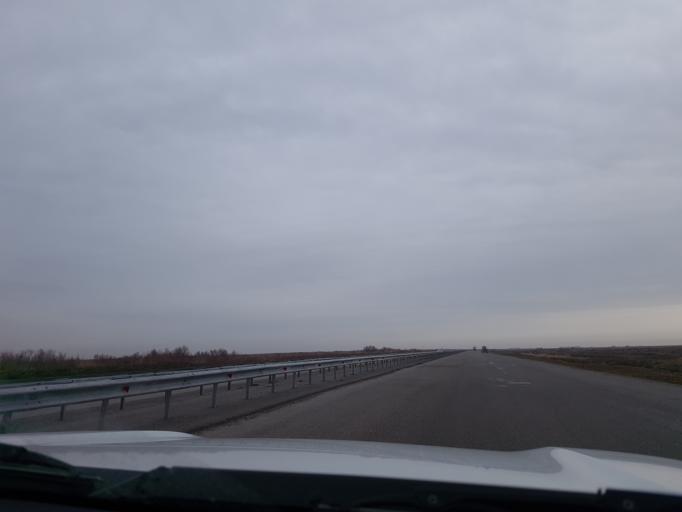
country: TM
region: Ahal
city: Tejen
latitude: 37.3539
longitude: 60.6260
